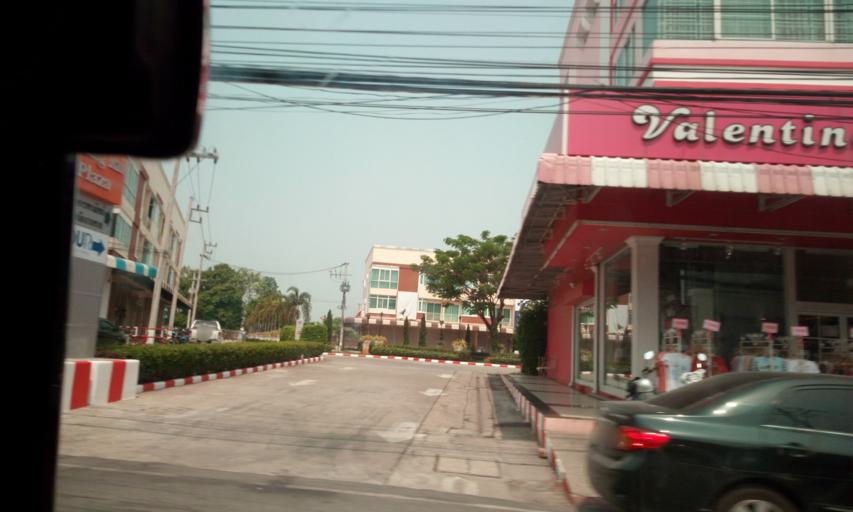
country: TH
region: Chiang Rai
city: Chiang Rai
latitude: 19.8905
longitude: 99.8304
